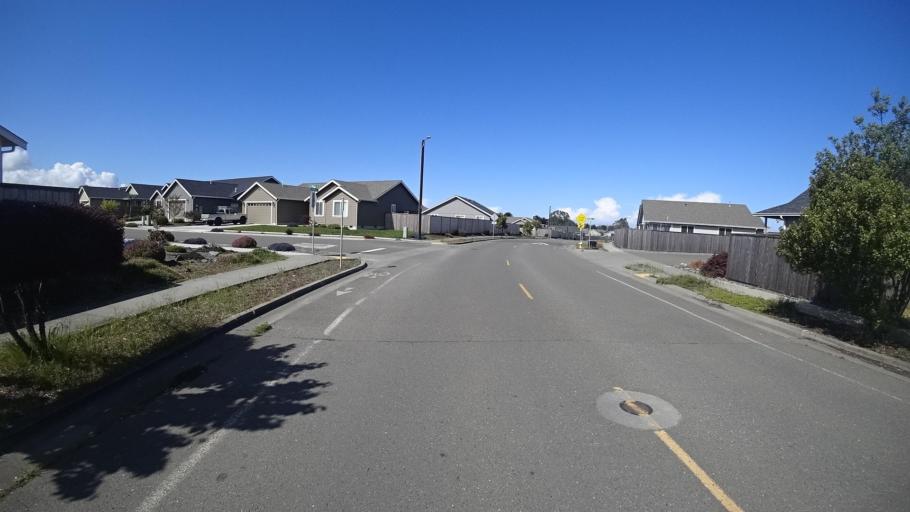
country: US
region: California
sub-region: Humboldt County
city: McKinleyville
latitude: 40.9389
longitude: -124.1054
